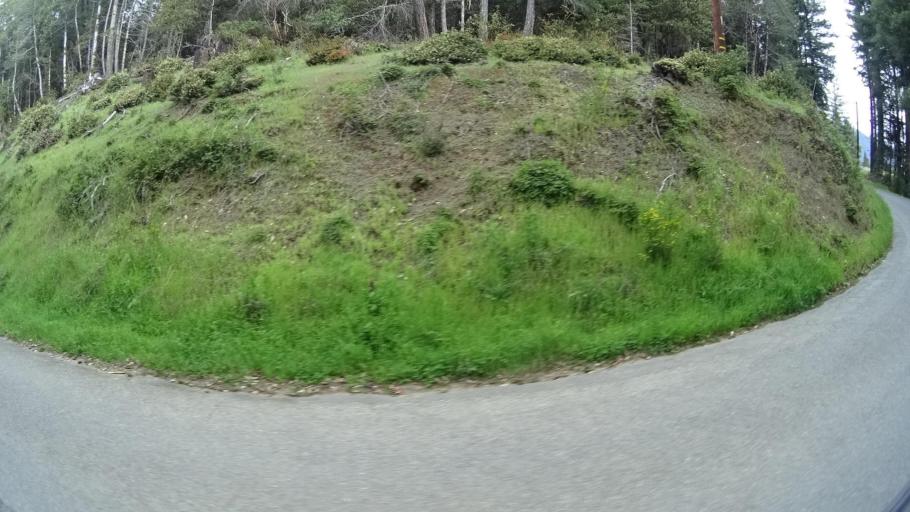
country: US
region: California
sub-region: Humboldt County
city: Redway
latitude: 40.3072
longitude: -123.8182
